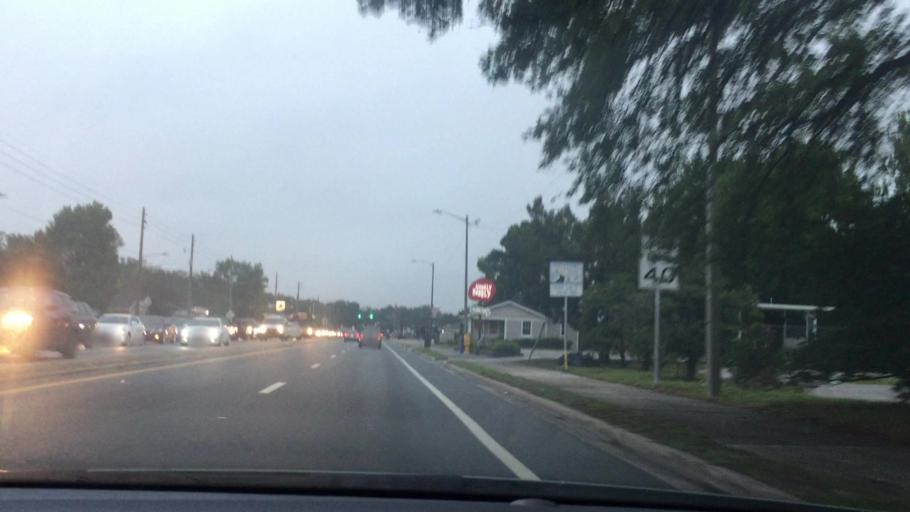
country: US
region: Florida
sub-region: Orange County
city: Fairview Shores
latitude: 28.5823
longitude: -81.3897
